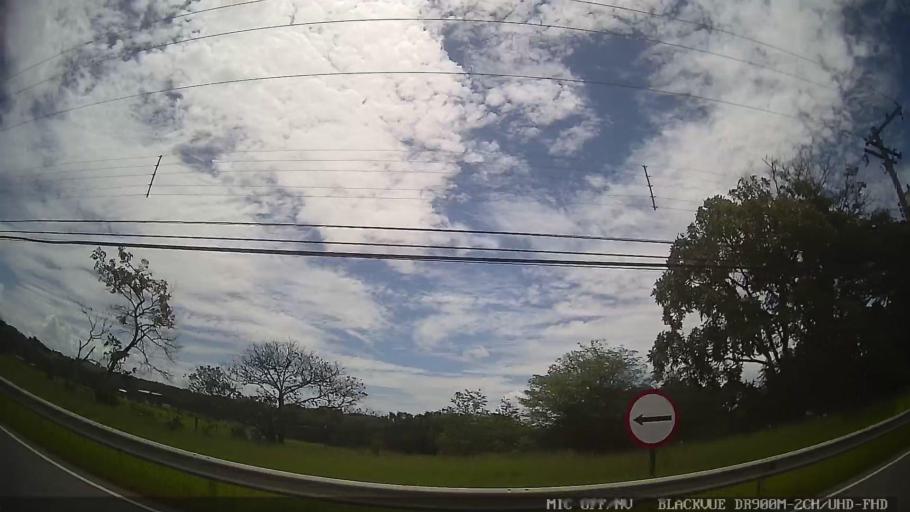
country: BR
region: Sao Paulo
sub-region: Conchas
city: Conchas
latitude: -23.0666
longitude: -47.9742
